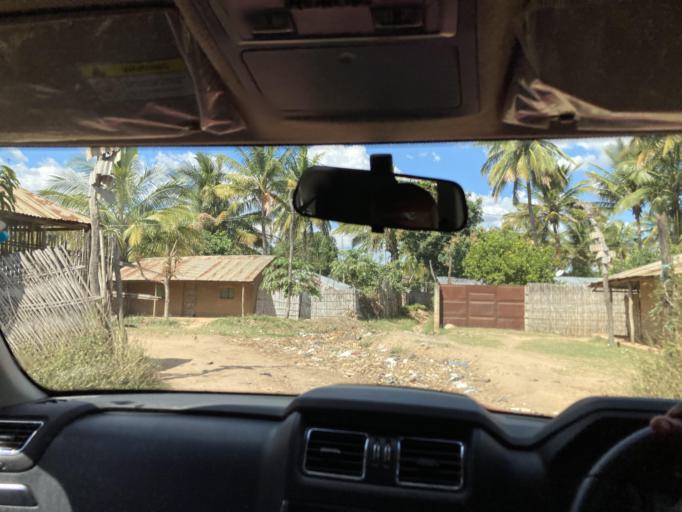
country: MZ
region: Cabo Delgado
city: Montepuez
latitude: -13.1364
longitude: 39.0027
